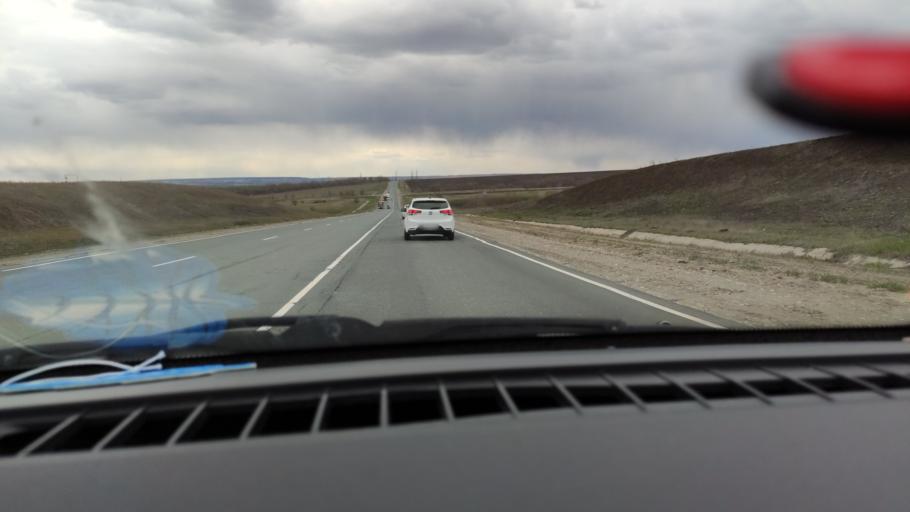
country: RU
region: Saratov
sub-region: Saratovskiy Rayon
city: Saratov
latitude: 51.7552
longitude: 46.0646
